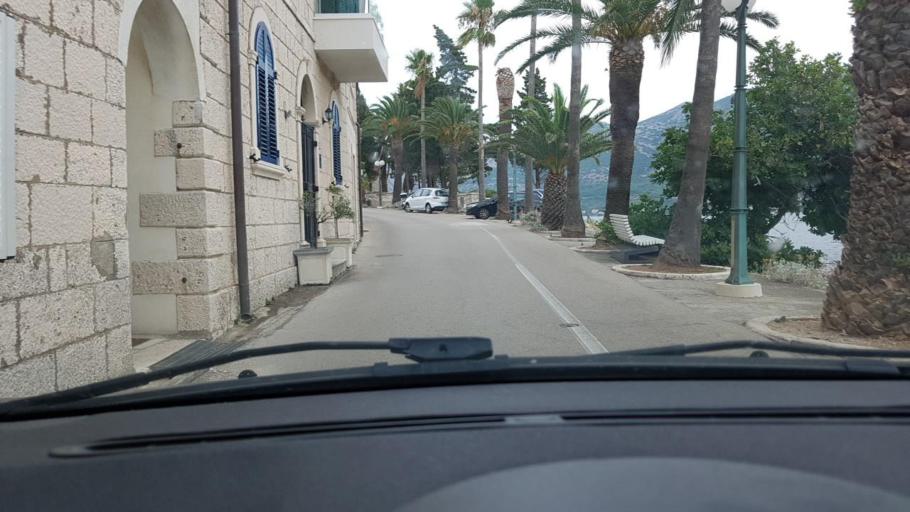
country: HR
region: Dubrovacko-Neretvanska
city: Korcula
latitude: 42.9622
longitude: 17.1309
